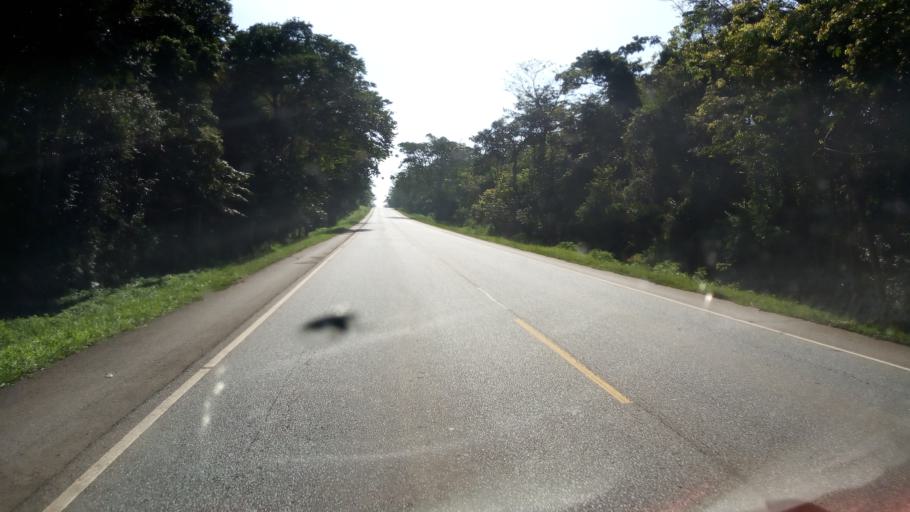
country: UG
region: Eastern Region
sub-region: Busia District
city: Busia
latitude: 0.5348
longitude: 33.9957
